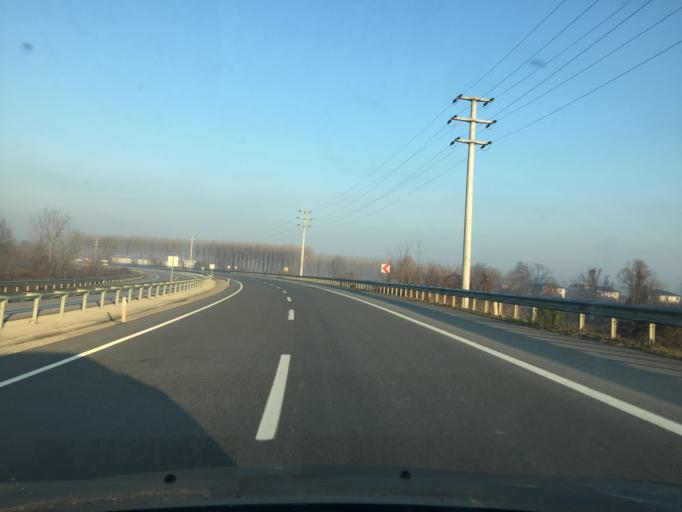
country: TR
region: Sakarya
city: Akyazi
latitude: 40.6448
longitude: 30.6127
